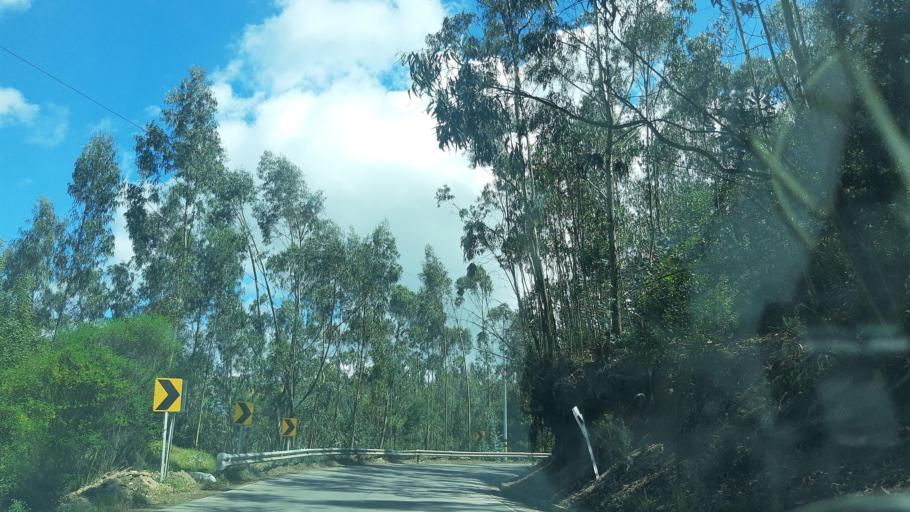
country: CO
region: Boyaca
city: Samaca
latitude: 5.4826
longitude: -73.4717
